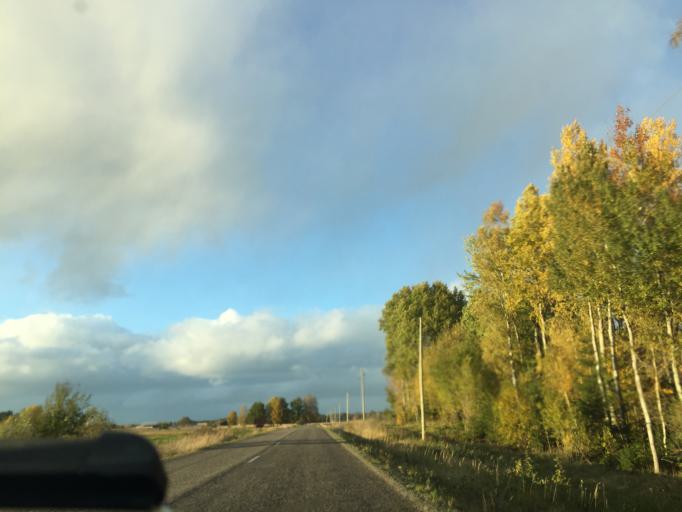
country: LV
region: Broceni
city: Broceni
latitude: 56.8714
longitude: 22.3814
